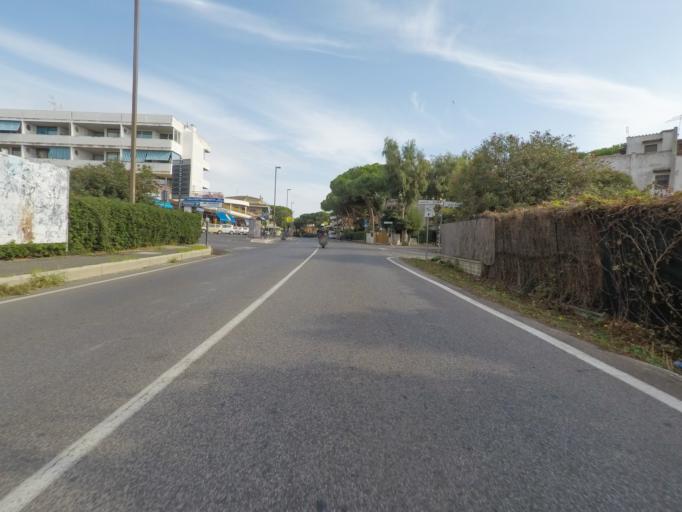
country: IT
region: Latium
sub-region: Citta metropolitana di Roma Capitale
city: Santa Marinella
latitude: 42.0335
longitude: 11.8366
